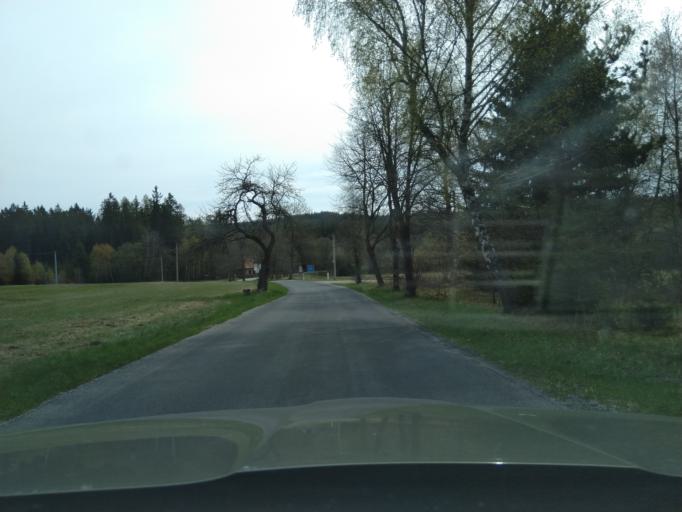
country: CZ
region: Jihocesky
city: Vacov
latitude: 49.1635
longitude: 13.6852
